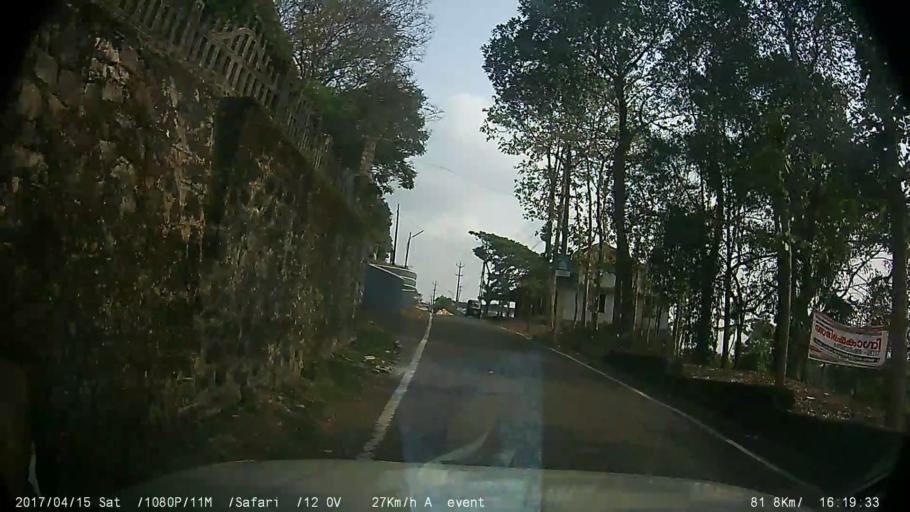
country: IN
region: Kerala
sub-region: Kottayam
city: Kottayam
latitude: 9.6471
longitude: 76.5193
